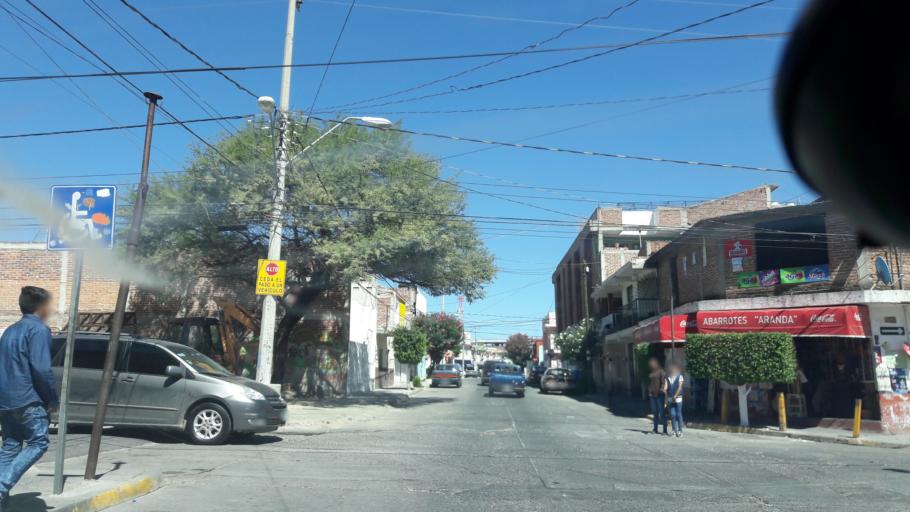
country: MX
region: Guanajuato
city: Leon
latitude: 21.1104
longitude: -101.6968
